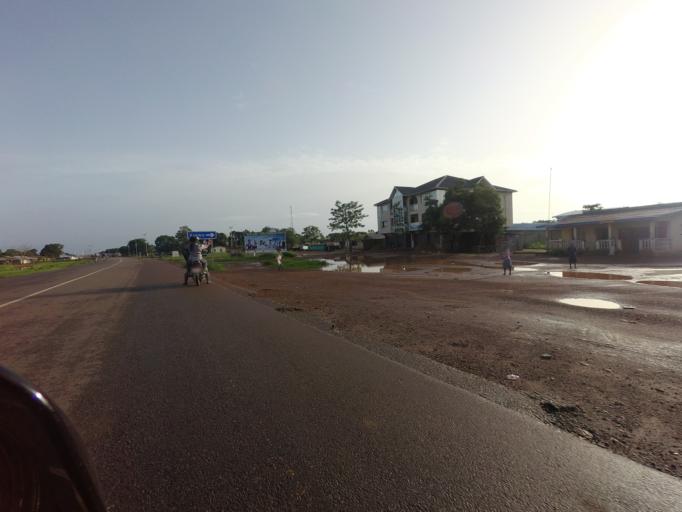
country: SL
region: Northern Province
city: Kambia
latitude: 9.1069
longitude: -12.9238
